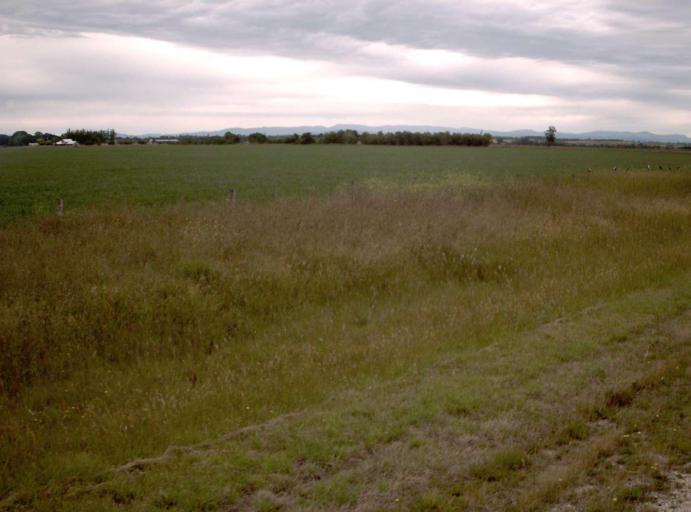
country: AU
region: Victoria
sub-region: Wellington
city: Sale
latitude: -38.0460
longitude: 147.1752
